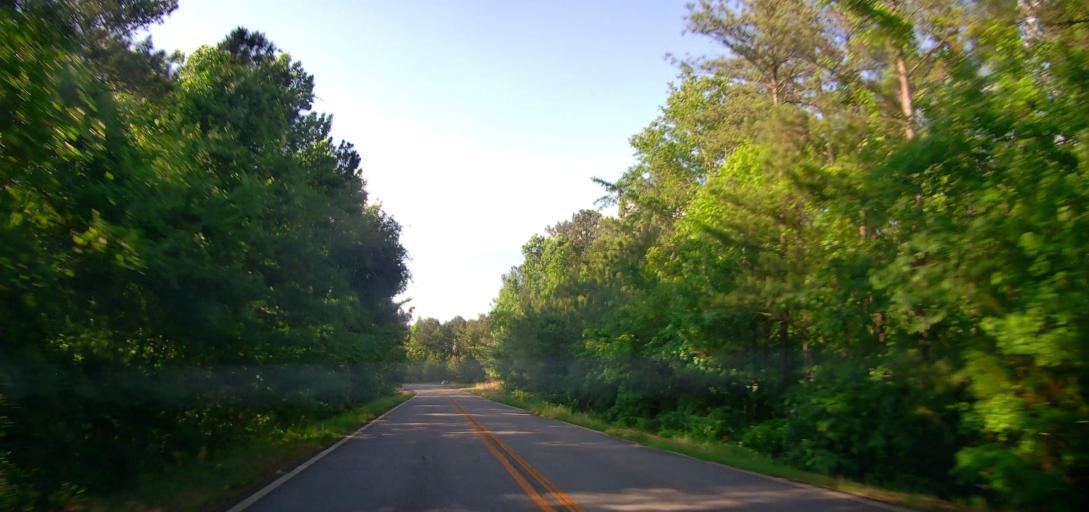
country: US
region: Georgia
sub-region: Peach County
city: Byron
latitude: 32.6780
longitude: -83.7641
